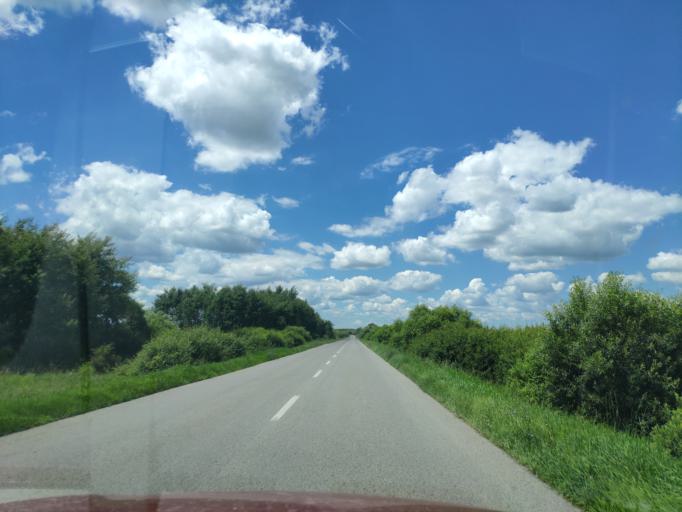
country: HU
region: Borsod-Abauj-Zemplen
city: Ozd
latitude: 48.3095
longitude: 20.2615
